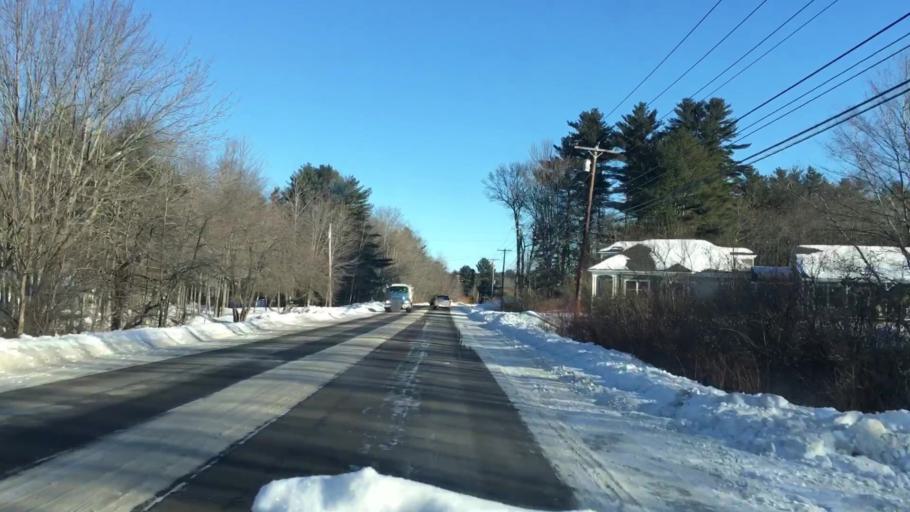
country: US
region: Maine
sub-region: Cumberland County
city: Brunswick
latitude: 43.9442
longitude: -69.9291
